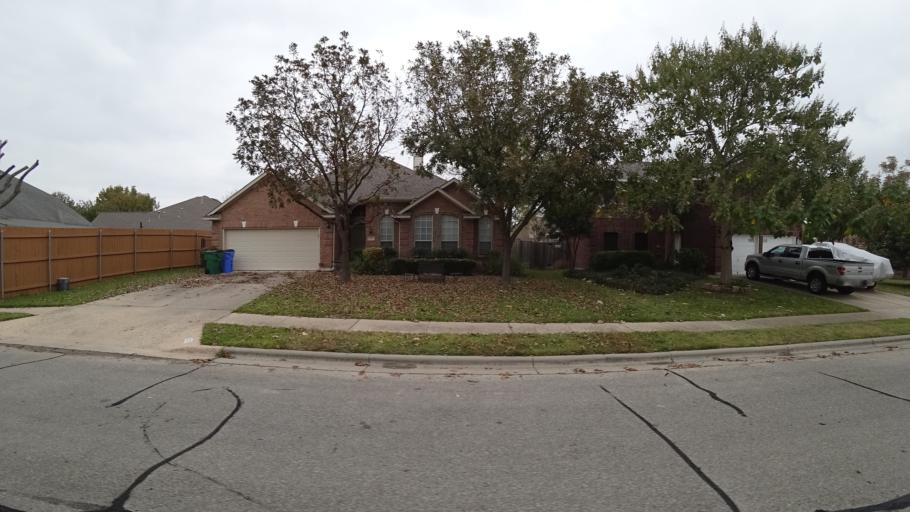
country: US
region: Texas
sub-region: Travis County
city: Pflugerville
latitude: 30.4327
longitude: -97.6234
